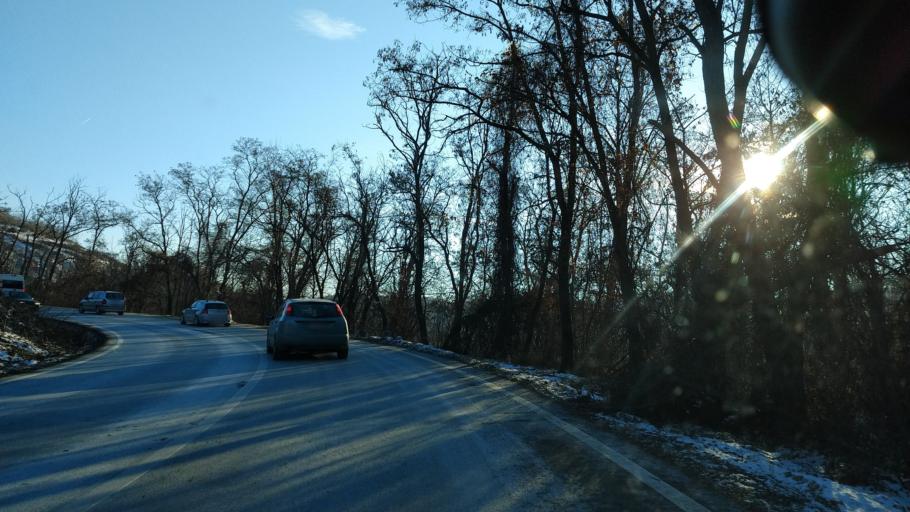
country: RO
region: Bacau
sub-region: Comuna Luizi-Calugara
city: Luizi-Calugara
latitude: 46.5439
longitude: 26.8177
